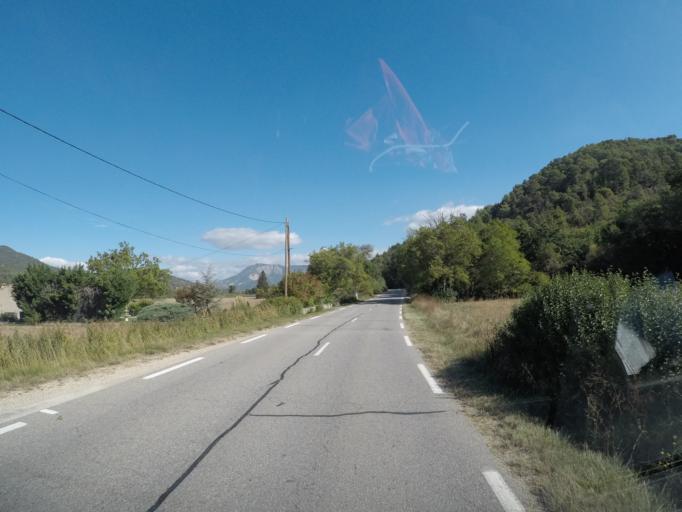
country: FR
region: Provence-Alpes-Cote d'Azur
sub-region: Departement des Alpes-de-Haute-Provence
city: Mallemoisson
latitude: 43.9461
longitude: 6.1740
